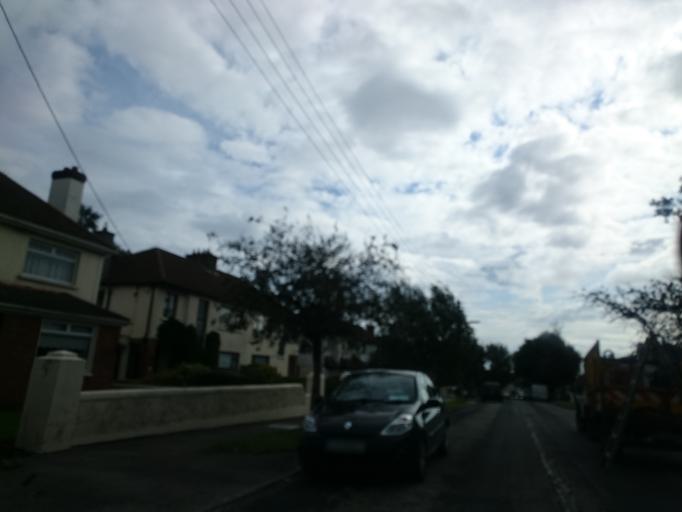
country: IE
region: Leinster
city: Mount Merrion
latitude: 53.2938
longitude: -6.2129
